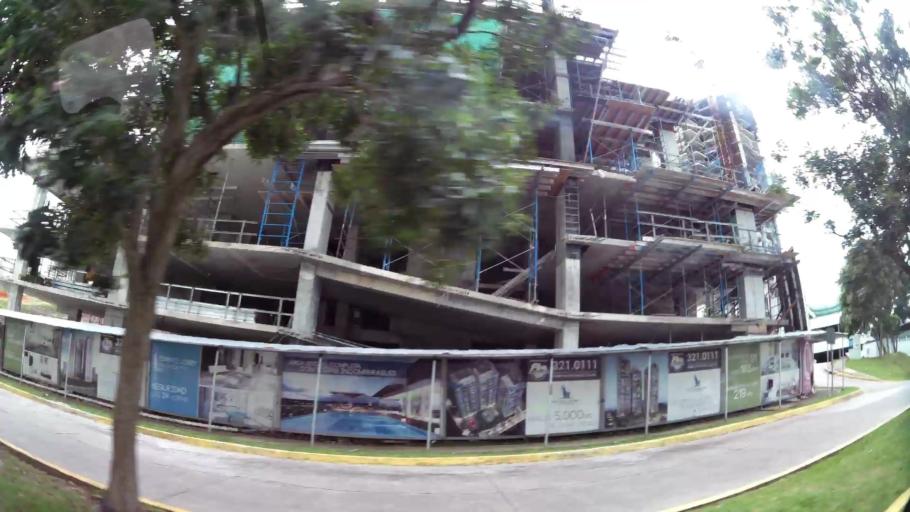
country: PA
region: Panama
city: Panama
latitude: 8.9951
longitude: -79.5306
